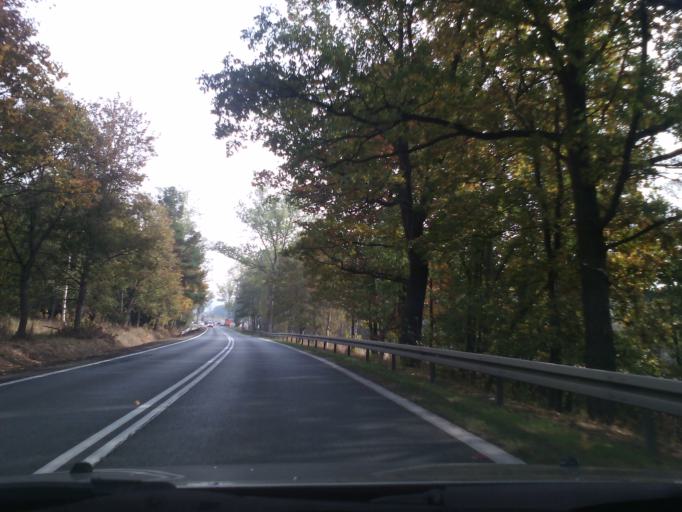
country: PL
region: Lower Silesian Voivodeship
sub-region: Powiat jeleniogorski
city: Janowice Wielkie
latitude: 50.9009
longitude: 15.8721
